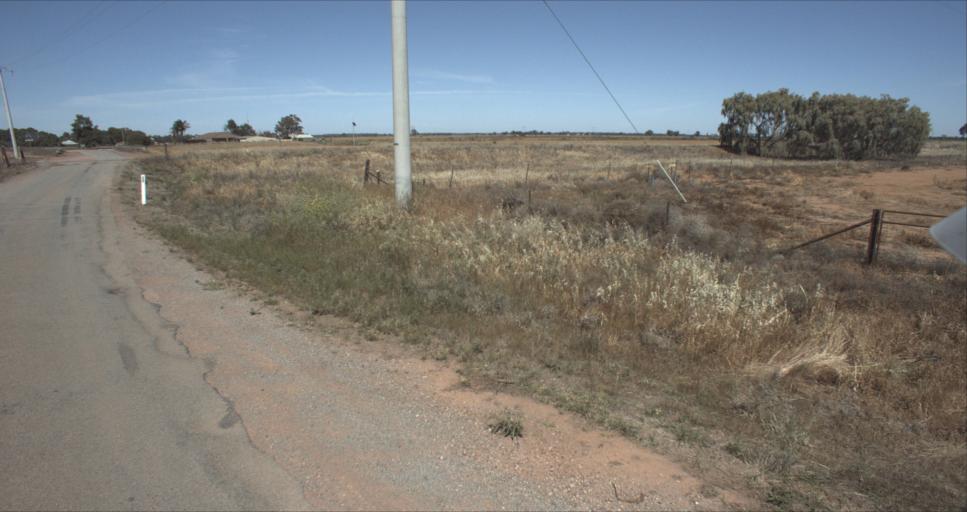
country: AU
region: New South Wales
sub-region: Leeton
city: Leeton
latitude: -34.5668
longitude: 146.3116
